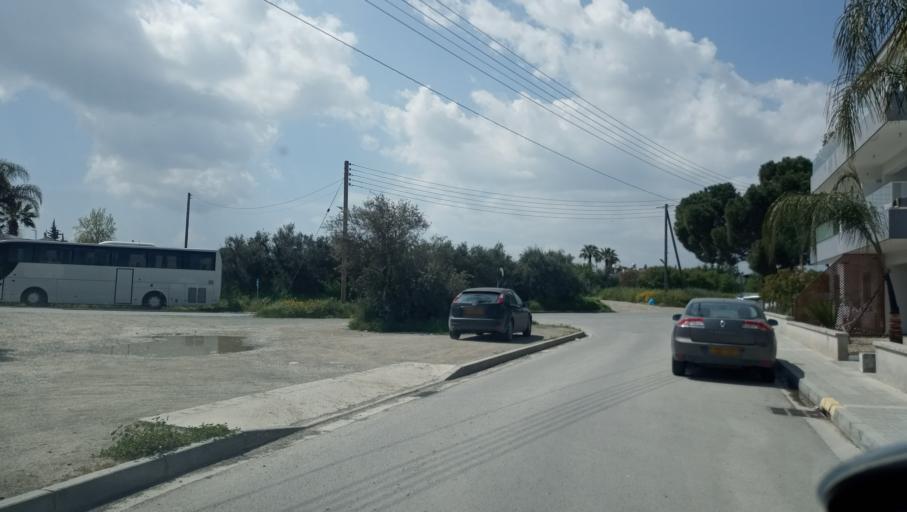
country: CY
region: Lefkosia
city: Dali
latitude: 35.0209
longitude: 33.4191
